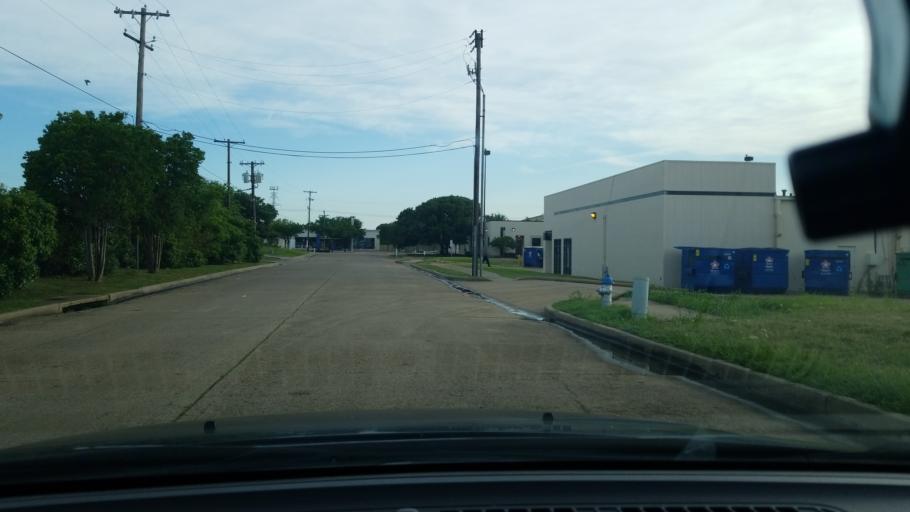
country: US
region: Texas
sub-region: Dallas County
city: Mesquite
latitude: 32.8094
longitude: -96.6146
